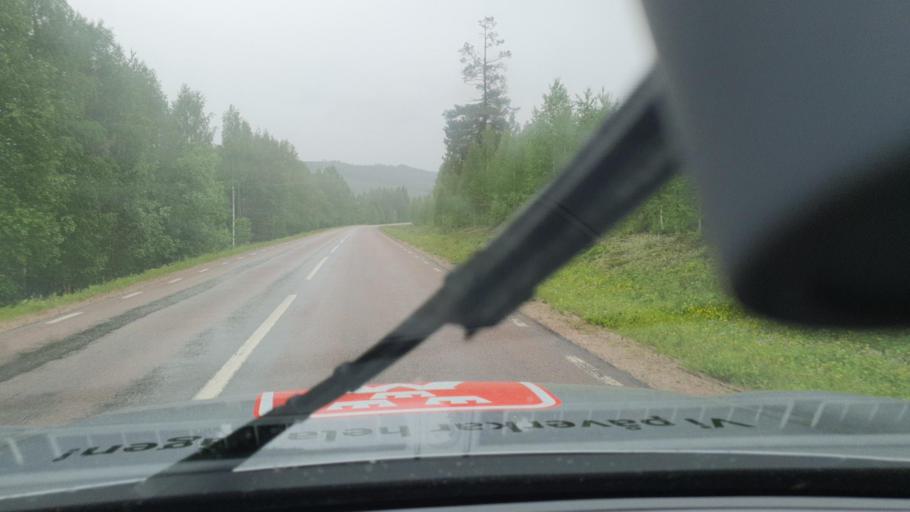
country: SE
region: Norrbotten
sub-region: Overtornea Kommun
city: OEvertornea
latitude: 66.4262
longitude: 23.3465
